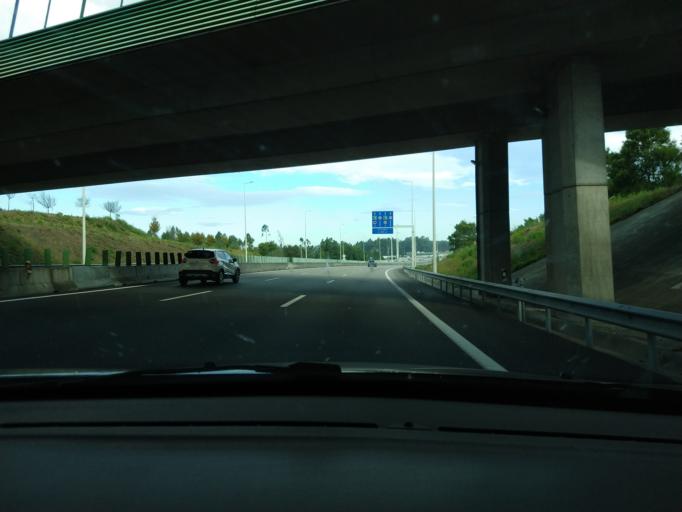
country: PT
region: Aveiro
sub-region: Santa Maria da Feira
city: Nogueira da Regedoura
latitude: 41.0112
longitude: -8.5827
